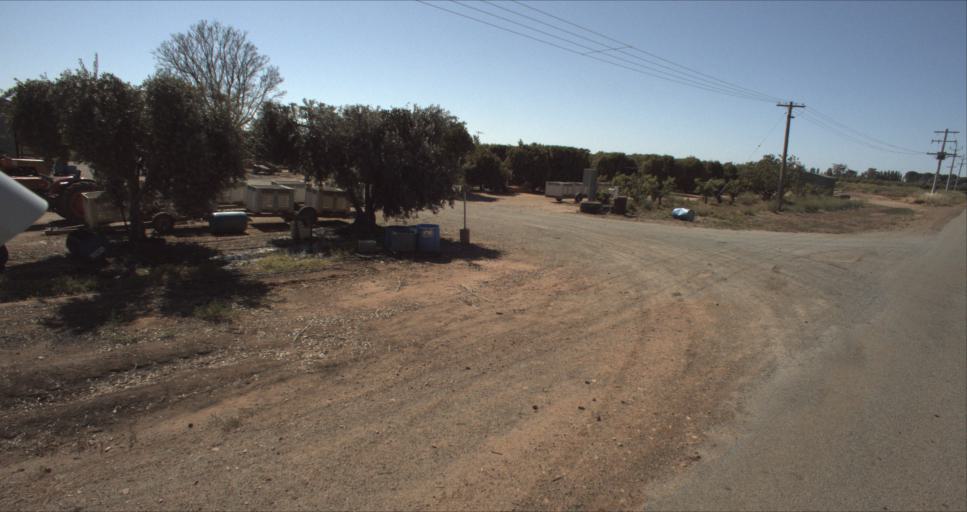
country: AU
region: New South Wales
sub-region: Leeton
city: Leeton
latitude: -34.5373
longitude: 146.3339
